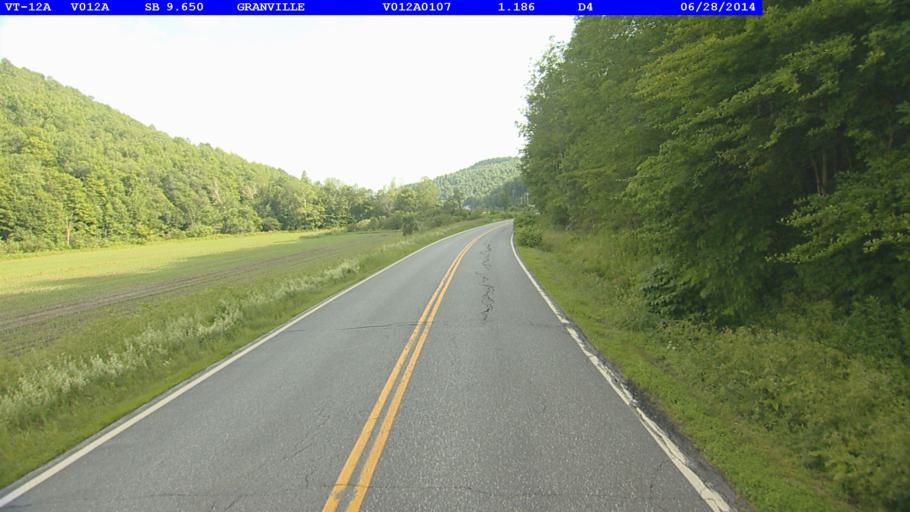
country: US
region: Vermont
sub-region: Orange County
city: Randolph
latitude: 44.0271
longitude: -72.7594
